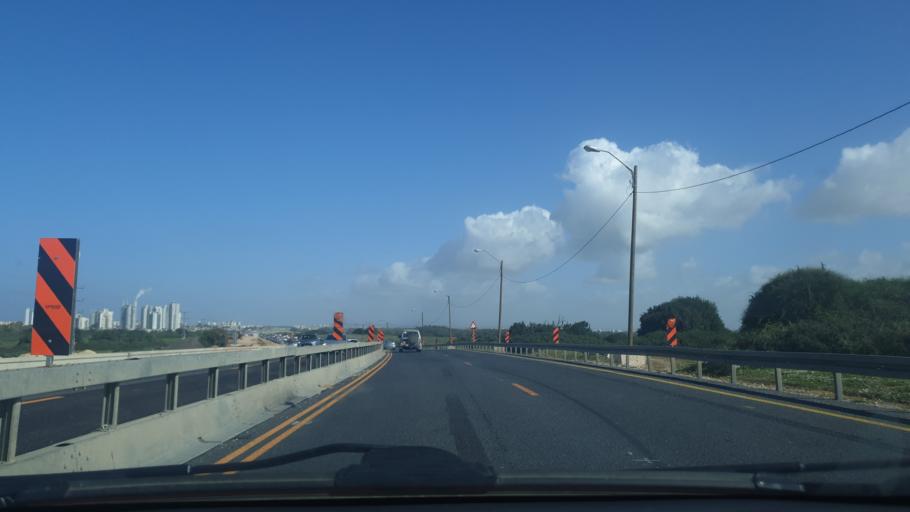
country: IL
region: Haifa
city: Hadera
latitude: 32.4086
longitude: 34.8824
